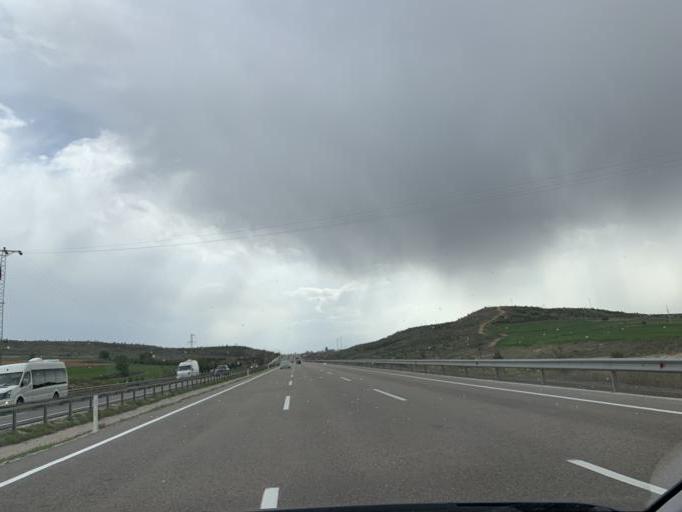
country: TR
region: Eskisehir
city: Sivrihisar
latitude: 39.5169
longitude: 31.6182
